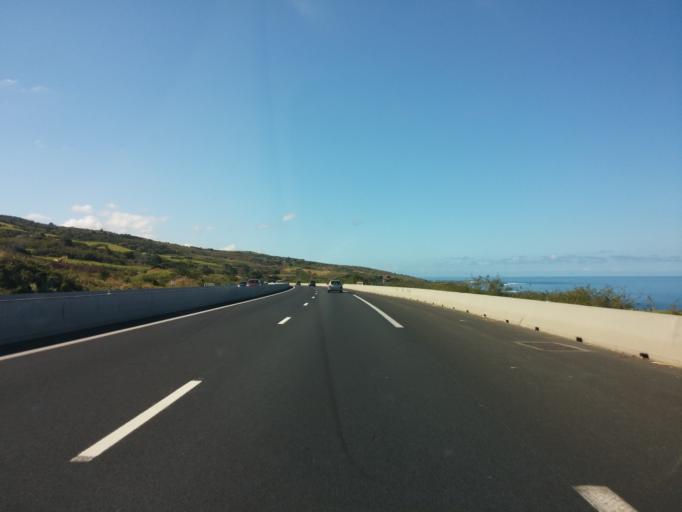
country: RE
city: Piton Saint-Leu
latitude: -21.2261
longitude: 55.3051
